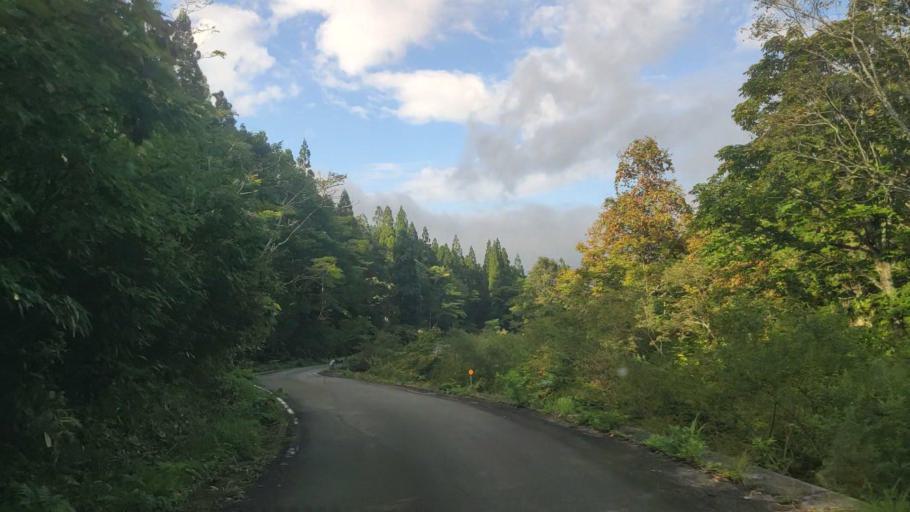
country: JP
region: Toyama
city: Yatsuomachi-higashikumisaka
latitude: 36.3664
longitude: 137.0751
